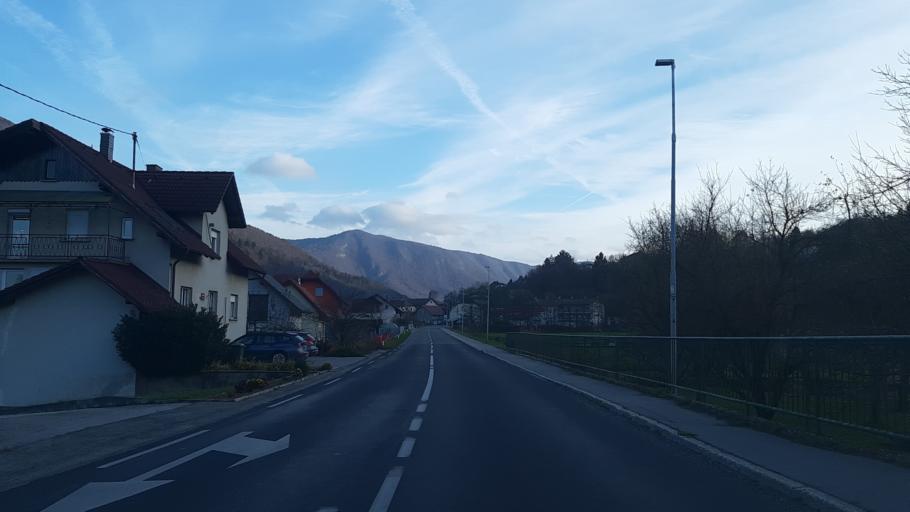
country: SI
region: Borovnica
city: Borovnica
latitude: 45.9234
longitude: 14.3583
